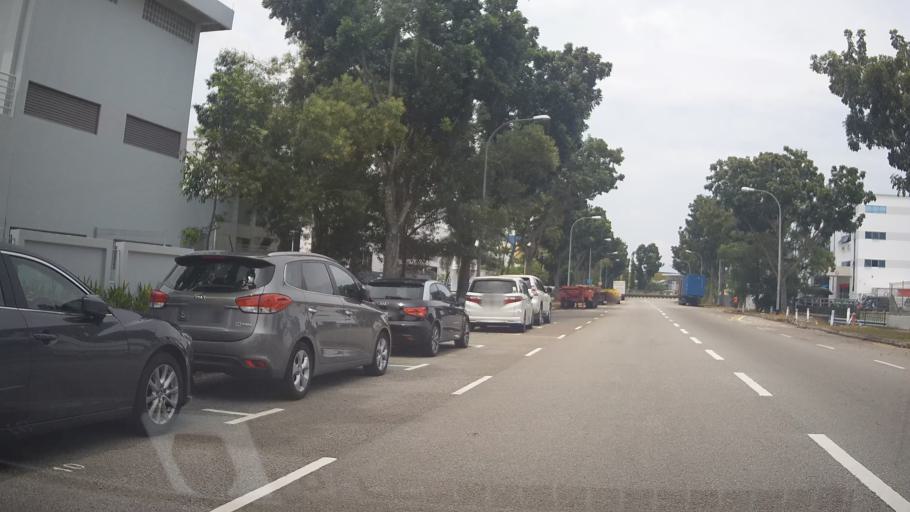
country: SG
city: Singapore
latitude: 1.3369
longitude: 103.9708
